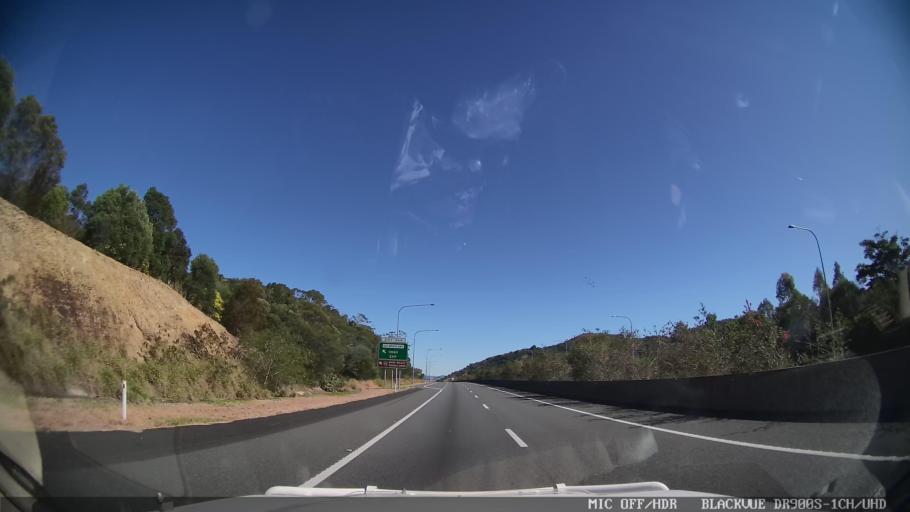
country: AU
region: Queensland
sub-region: Sunshine Coast
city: Black Mountain
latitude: -26.3895
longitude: 152.8045
